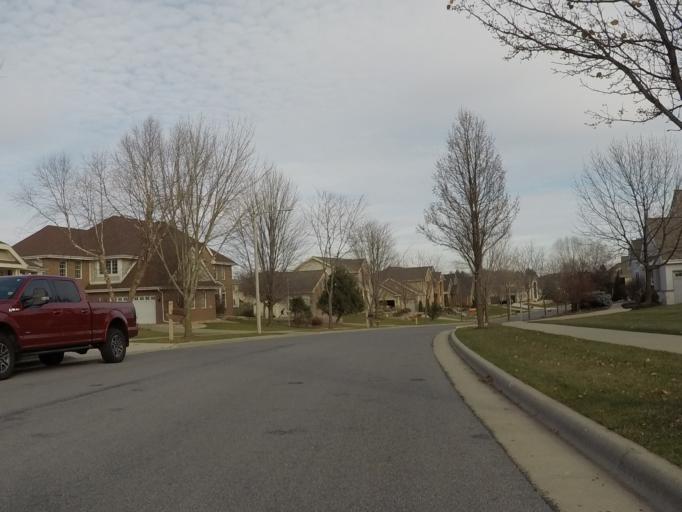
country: US
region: Wisconsin
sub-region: Dane County
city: Middleton
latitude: 43.0804
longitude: -89.5578
